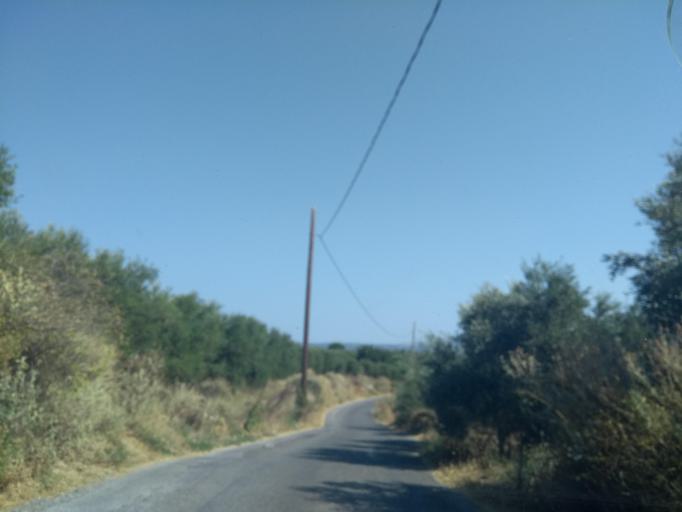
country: GR
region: Crete
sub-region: Nomos Chanias
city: Kalivai
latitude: 35.4319
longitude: 24.1760
